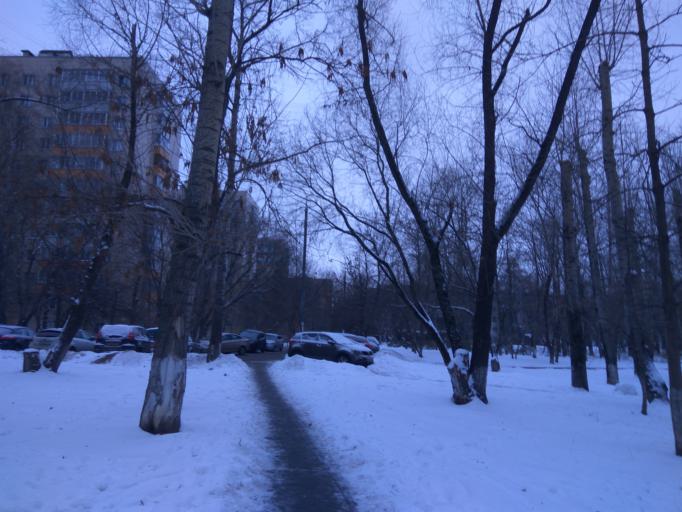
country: RU
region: Moscow
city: Tsaritsyno
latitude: 55.6364
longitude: 37.6515
